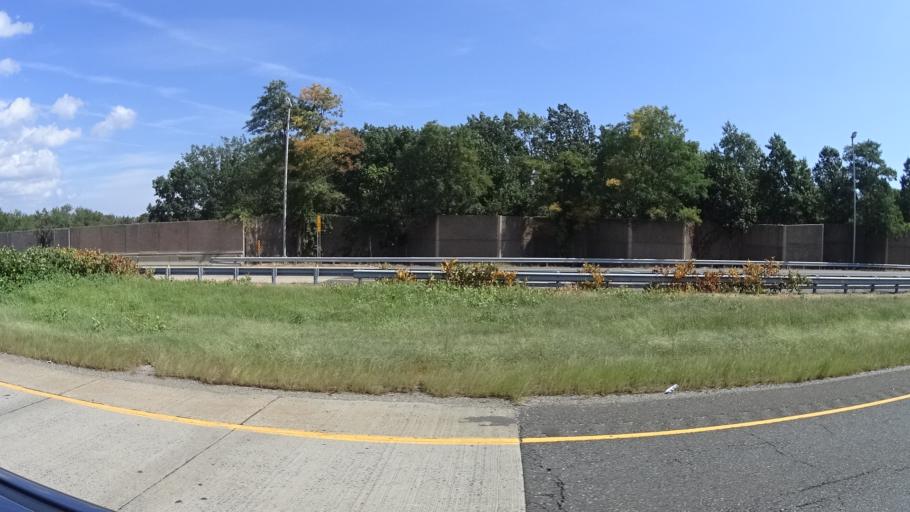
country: US
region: New Jersey
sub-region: Monmouth County
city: Eatontown
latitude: 40.2763
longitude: -74.0714
